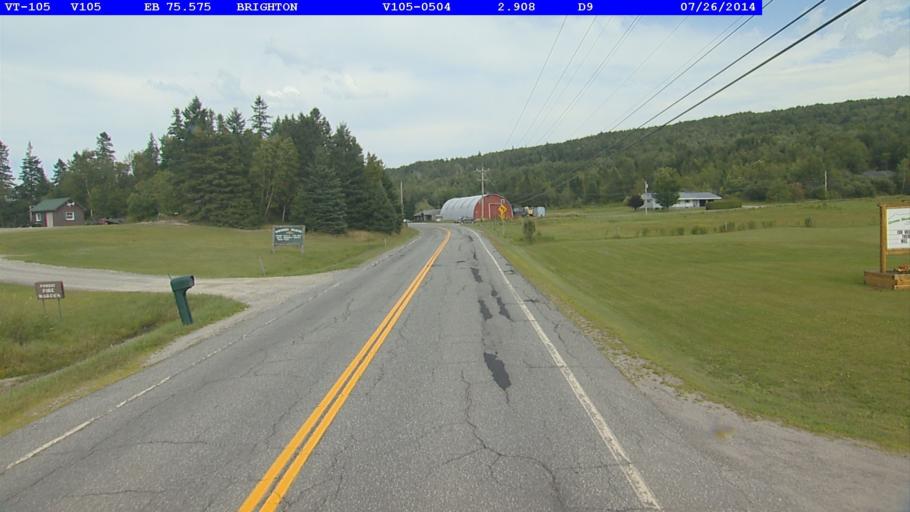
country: US
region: Vermont
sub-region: Caledonia County
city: Lyndonville
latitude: 44.8003
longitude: -71.8978
